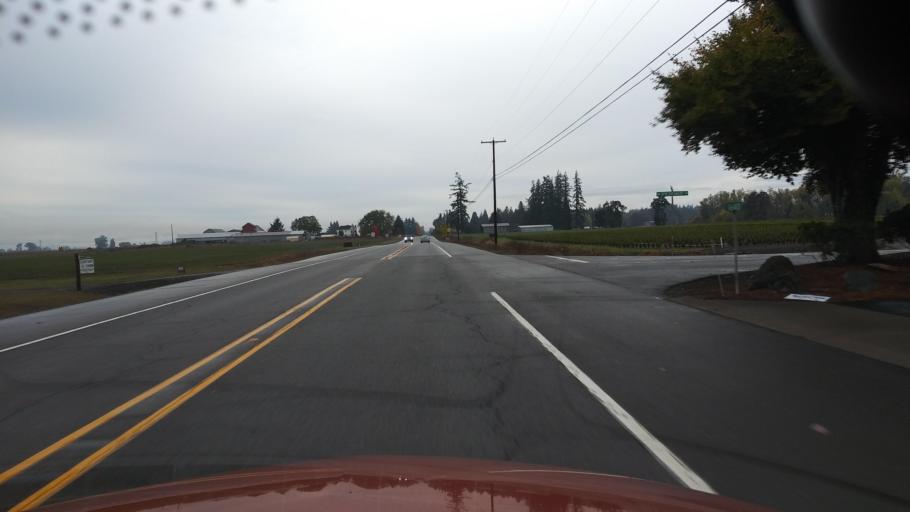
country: US
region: Oregon
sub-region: Washington County
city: Cornelius
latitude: 45.5318
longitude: -123.0597
